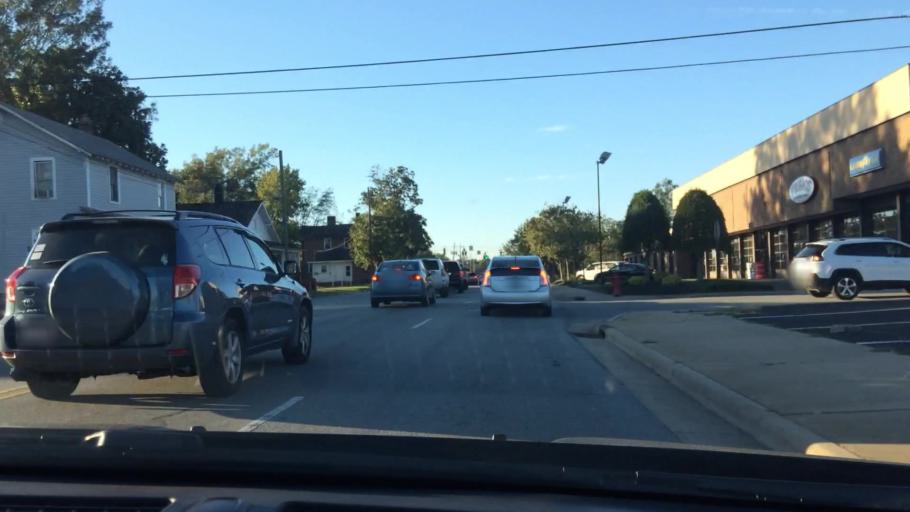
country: US
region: North Carolina
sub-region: Pitt County
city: Greenville
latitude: 35.6045
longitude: -77.3826
